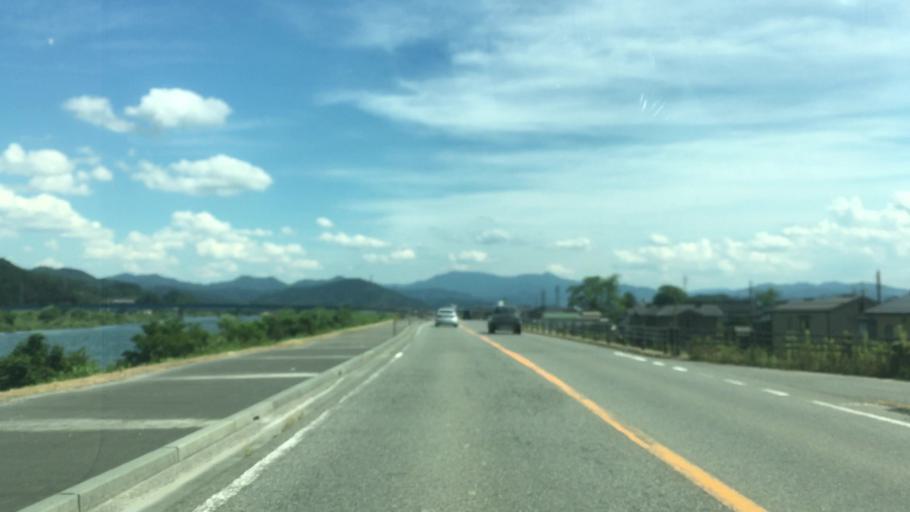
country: JP
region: Hyogo
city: Toyooka
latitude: 35.5620
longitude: 134.8135
